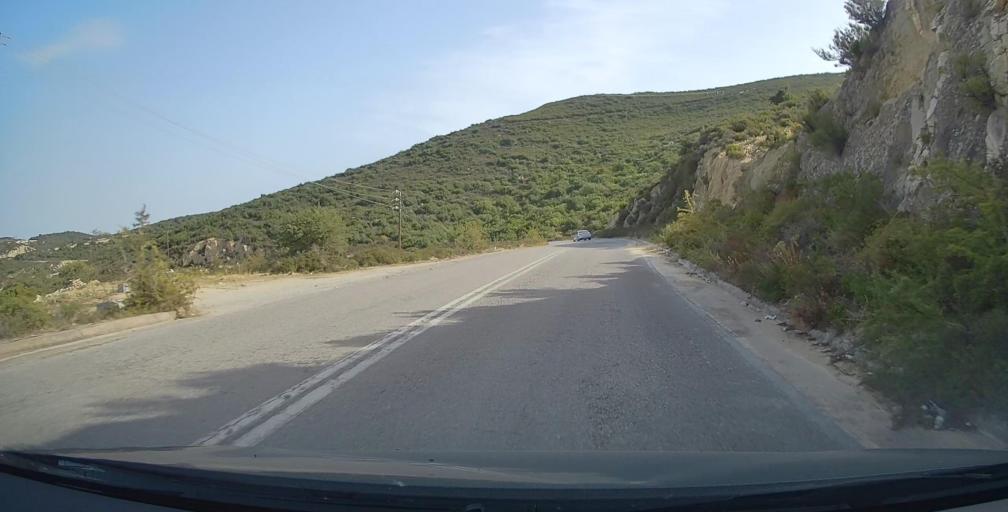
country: GR
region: Central Macedonia
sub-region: Nomos Chalkidikis
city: Sykia
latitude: 39.9752
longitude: 23.9588
